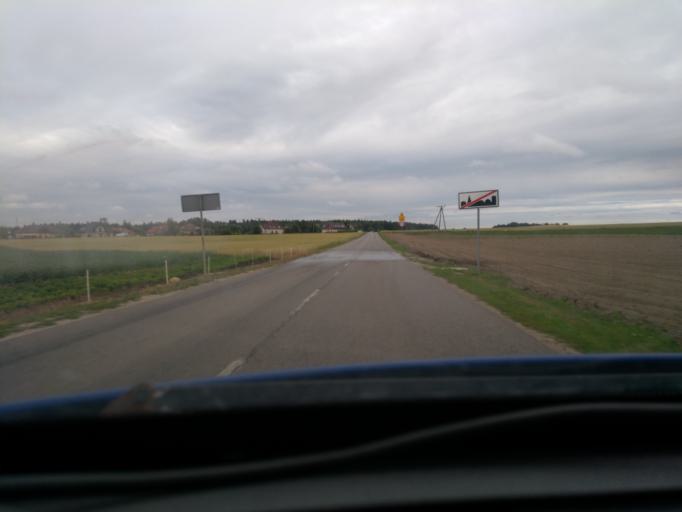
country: PL
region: Pomeranian Voivodeship
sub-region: Powiat kartuski
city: Banino
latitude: 54.3838
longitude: 18.4056
